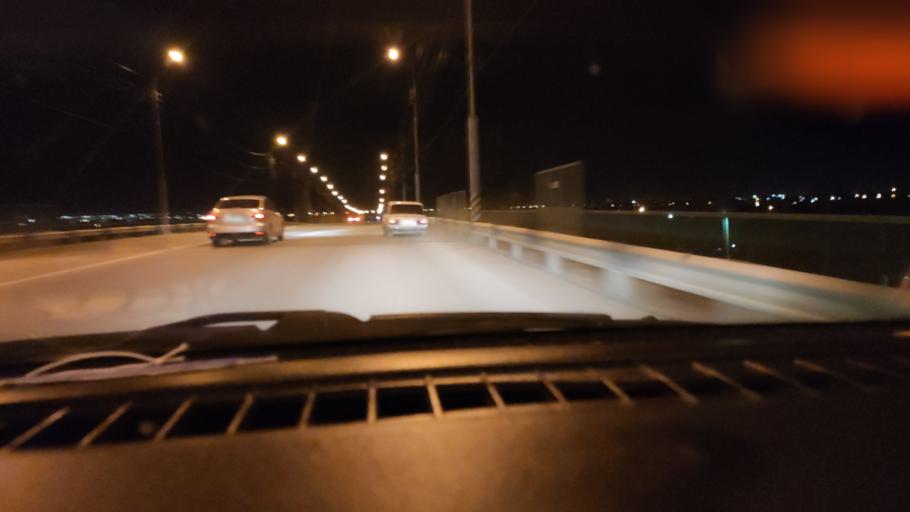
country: RU
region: Saratov
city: Privolzhskiy
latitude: 51.4161
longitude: 46.0452
